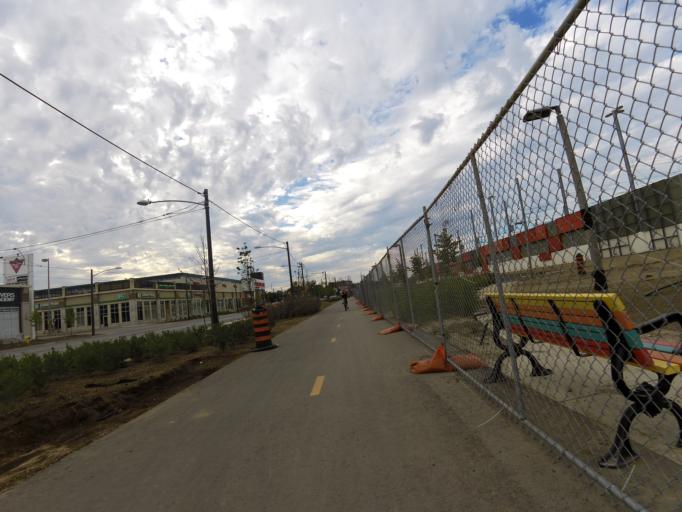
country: CA
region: Ontario
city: Toronto
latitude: 43.6575
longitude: -79.3269
